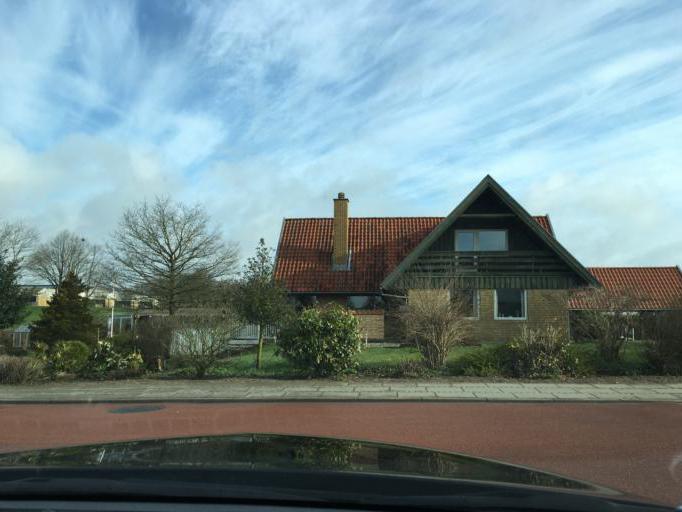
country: DK
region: South Denmark
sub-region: Kolding Kommune
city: Kolding
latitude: 55.4996
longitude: 9.4490
